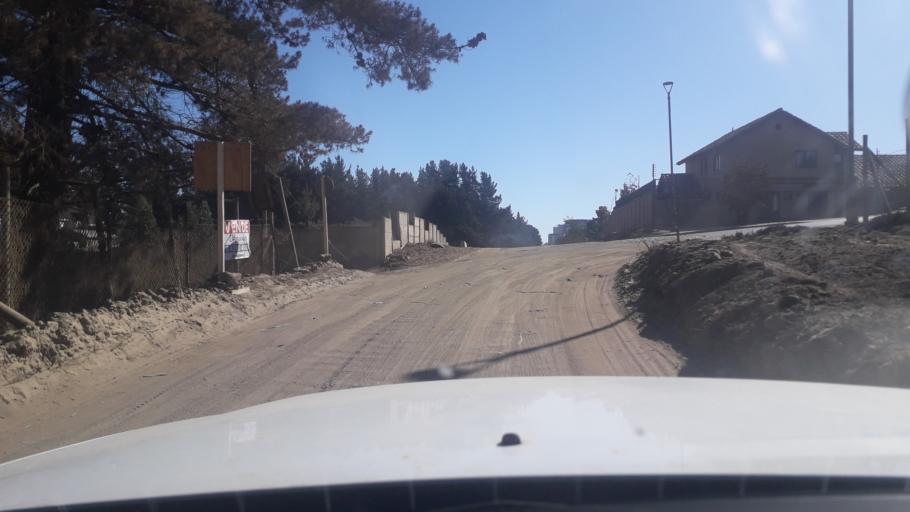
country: CL
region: Valparaiso
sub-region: Provincia de Valparaiso
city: Vina del Mar
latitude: -32.9527
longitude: -71.5337
